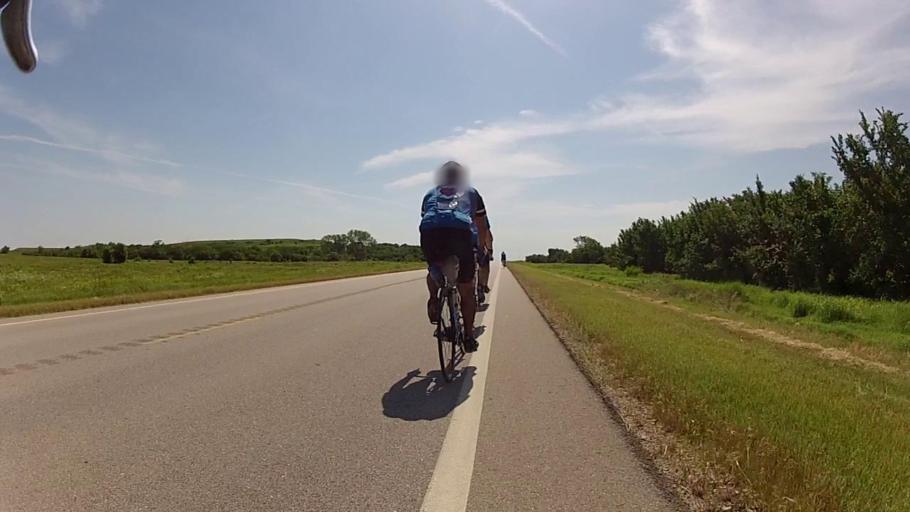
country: US
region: Kansas
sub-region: Chautauqua County
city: Sedan
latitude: 37.1072
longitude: -96.5771
